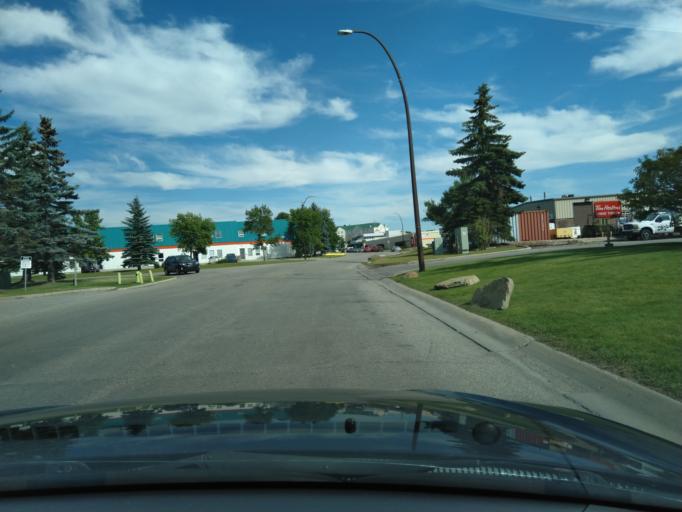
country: CA
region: Alberta
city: Calgary
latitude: 51.0940
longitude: -114.0105
